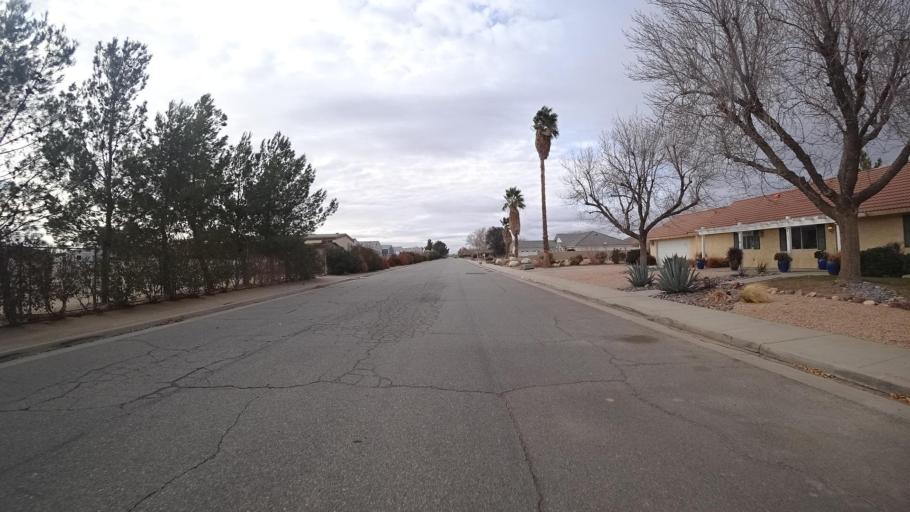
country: US
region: California
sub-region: Kern County
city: Rosamond
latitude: 34.8675
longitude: -118.2053
